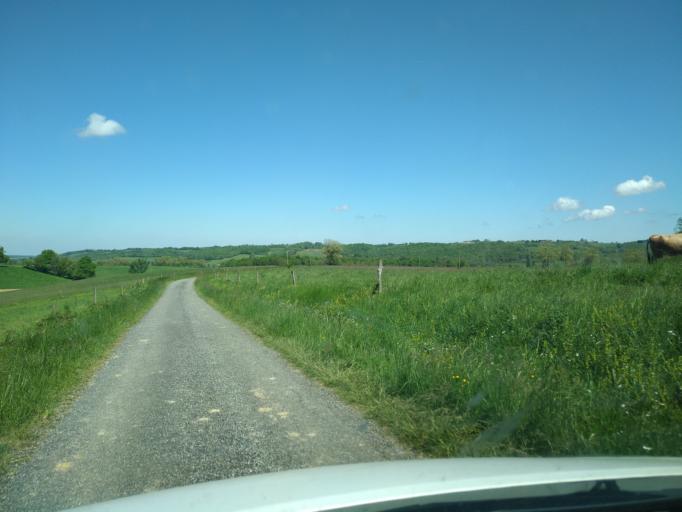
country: FR
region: Midi-Pyrenees
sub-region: Departement de la Haute-Garonne
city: Boulogne-sur-Gesse
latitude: 43.3030
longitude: 0.6693
